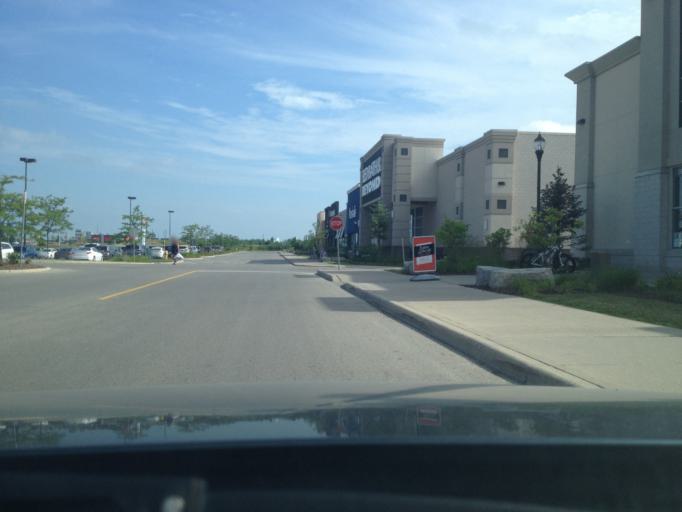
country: CA
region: Ontario
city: London
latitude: 42.9345
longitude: -81.2827
